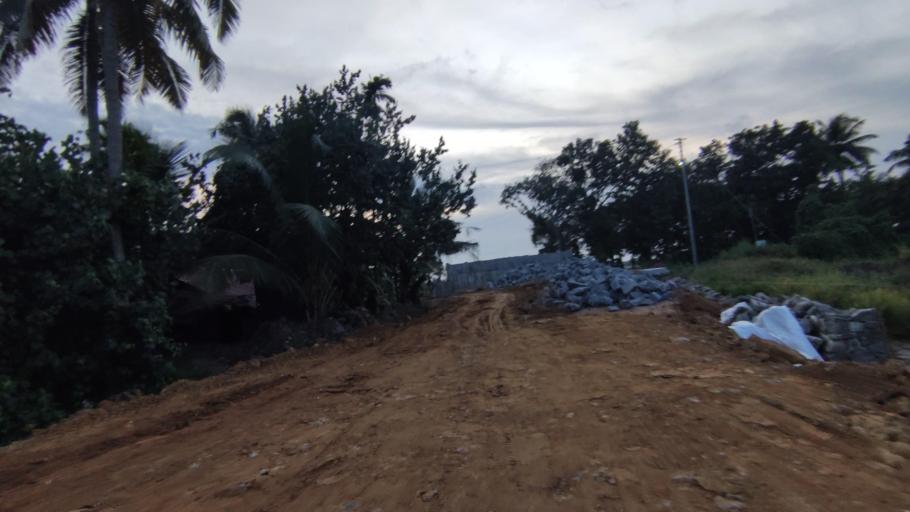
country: IN
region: Kerala
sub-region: Kottayam
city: Kottayam
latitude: 9.6471
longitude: 76.4652
